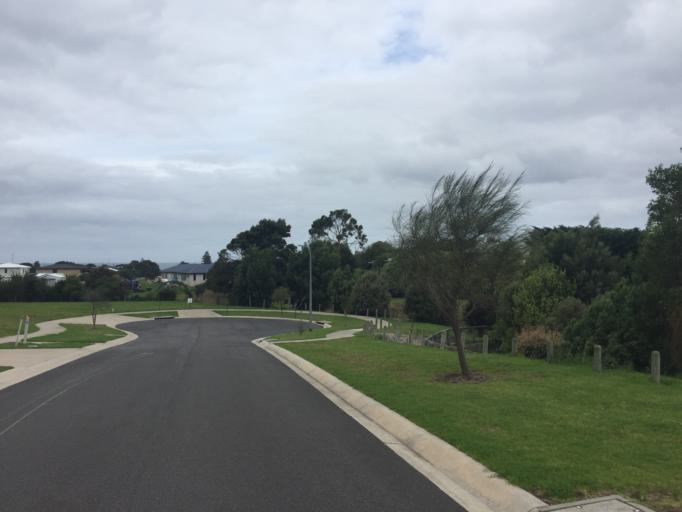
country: AU
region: Victoria
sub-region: Colac-Otway
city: Apollo Bay
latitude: -38.7474
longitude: 143.6641
